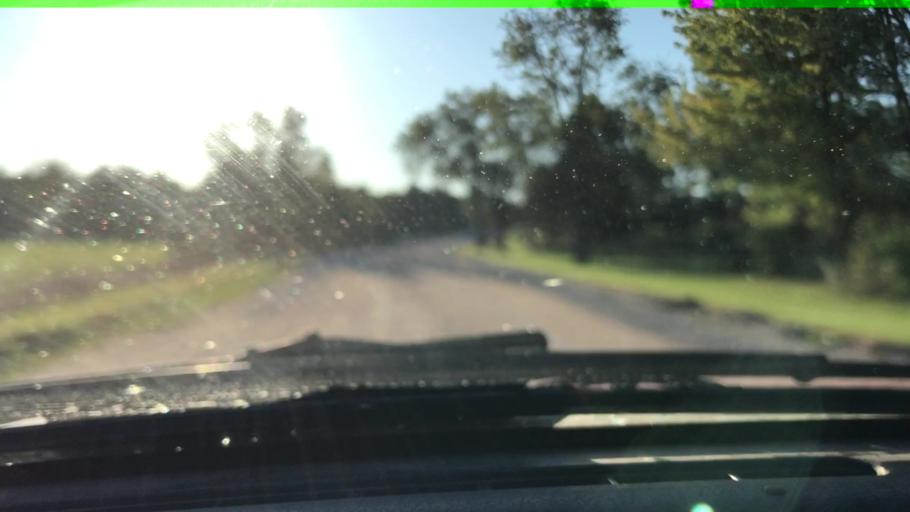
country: US
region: Nebraska
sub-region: Lancaster County
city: Lincoln
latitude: 40.7533
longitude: -96.7549
